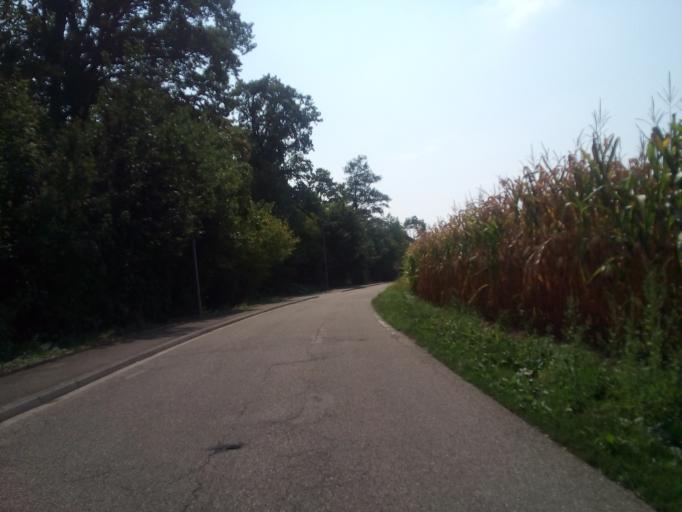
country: DE
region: Baden-Wuerttemberg
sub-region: Freiburg Region
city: Rheinau
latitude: 48.6241
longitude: 7.9067
